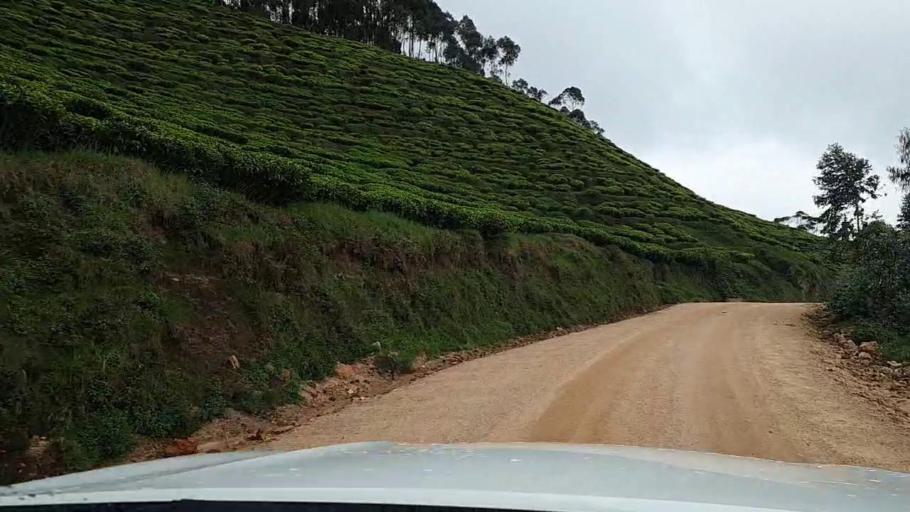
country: RW
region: Western Province
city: Kibuye
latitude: -2.2981
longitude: 29.3824
